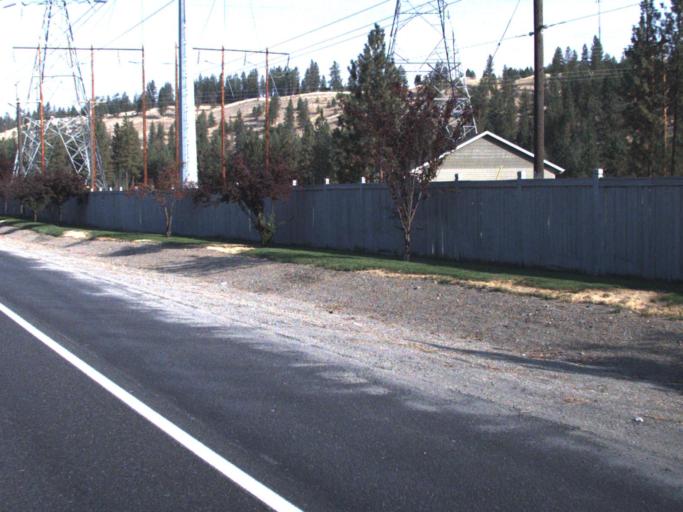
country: US
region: Washington
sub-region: Spokane County
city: Town and Country
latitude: 47.7527
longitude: -117.5130
